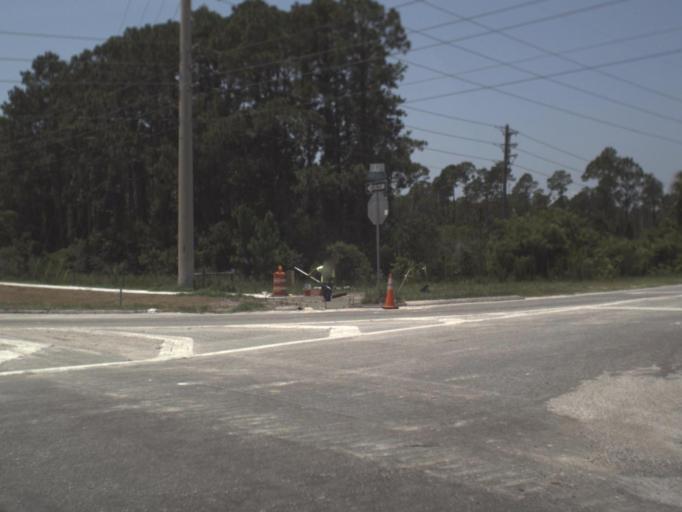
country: US
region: Florida
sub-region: Hernando County
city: Hernando Beach
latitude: 28.4156
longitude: -82.6489
